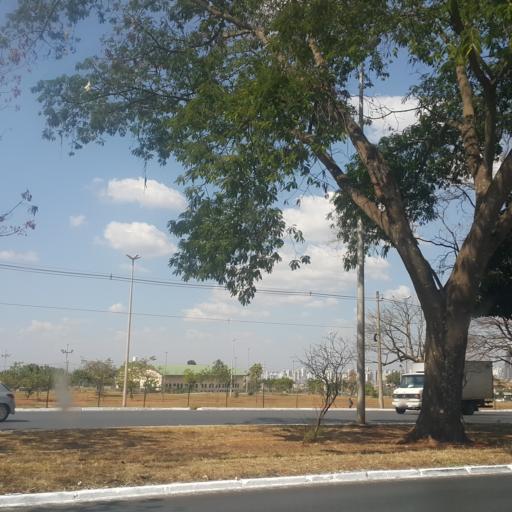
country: BR
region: Federal District
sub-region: Brasilia
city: Brasilia
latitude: -15.8160
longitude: -48.0582
